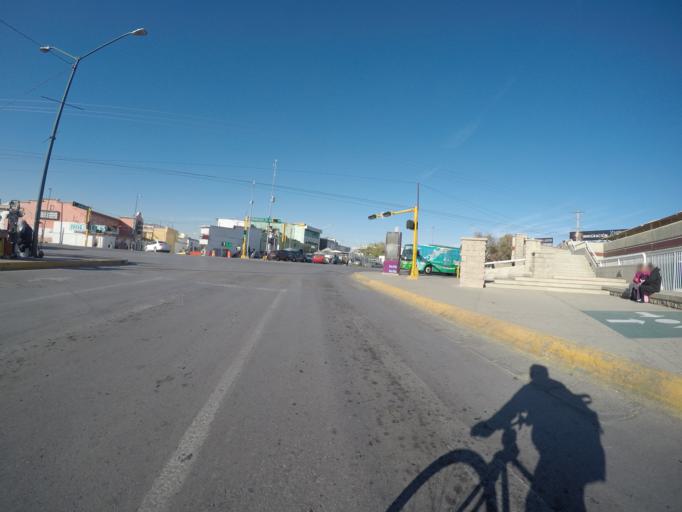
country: MX
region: Chihuahua
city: Ciudad Juarez
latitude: 31.7456
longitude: -106.4849
